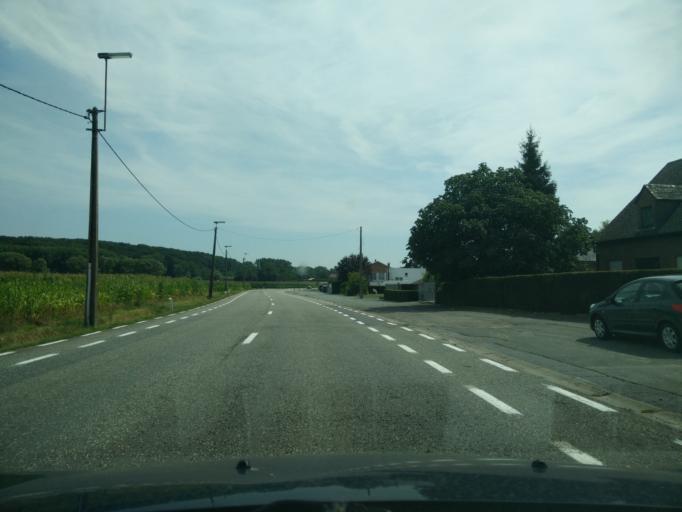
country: BE
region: Flanders
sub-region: Provincie Oost-Vlaanderen
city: Ninove
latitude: 50.8180
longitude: 4.0466
